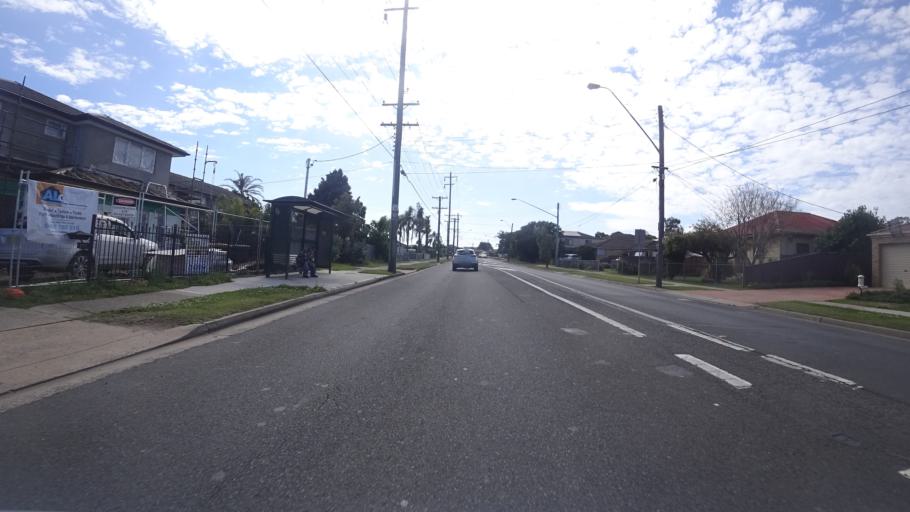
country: AU
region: New South Wales
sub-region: Bankstown
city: Milperra
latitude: -33.9429
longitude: 150.9502
